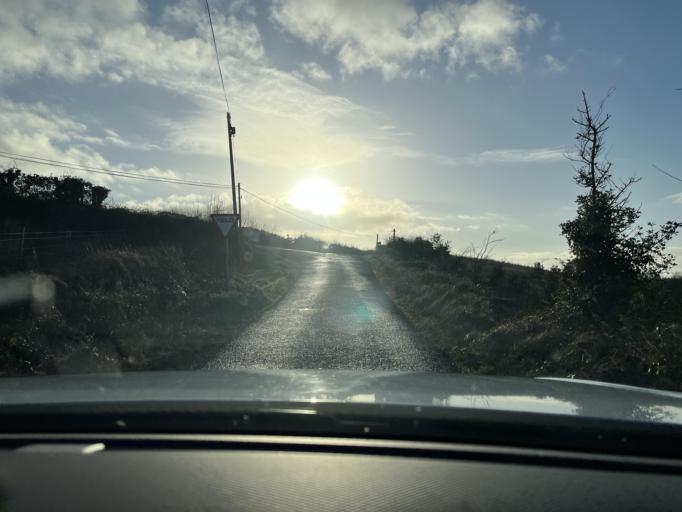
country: IE
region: Connaught
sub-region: County Leitrim
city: Manorhamilton
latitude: 54.2009
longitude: -7.9743
